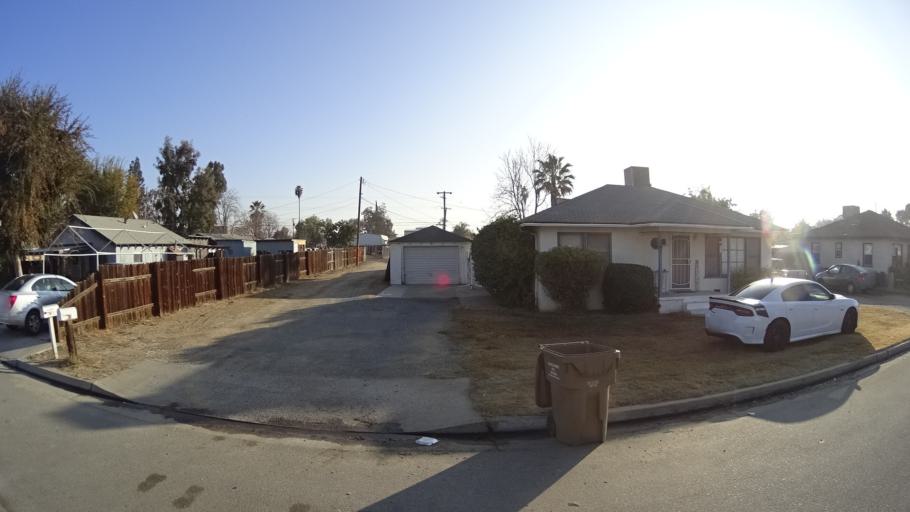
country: US
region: California
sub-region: Kern County
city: Greenacres
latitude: 35.3825
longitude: -119.1190
